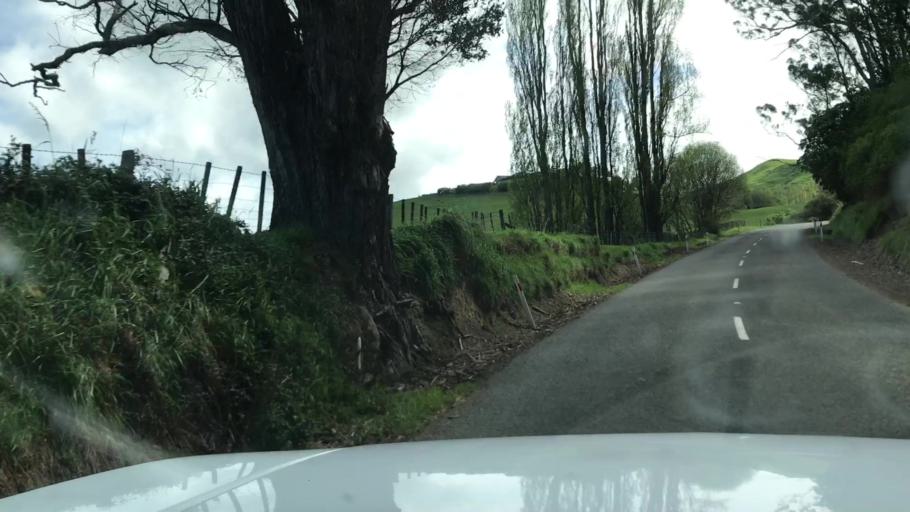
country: NZ
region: Hawke's Bay
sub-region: Hastings District
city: Hastings
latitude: -39.8155
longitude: 176.7502
